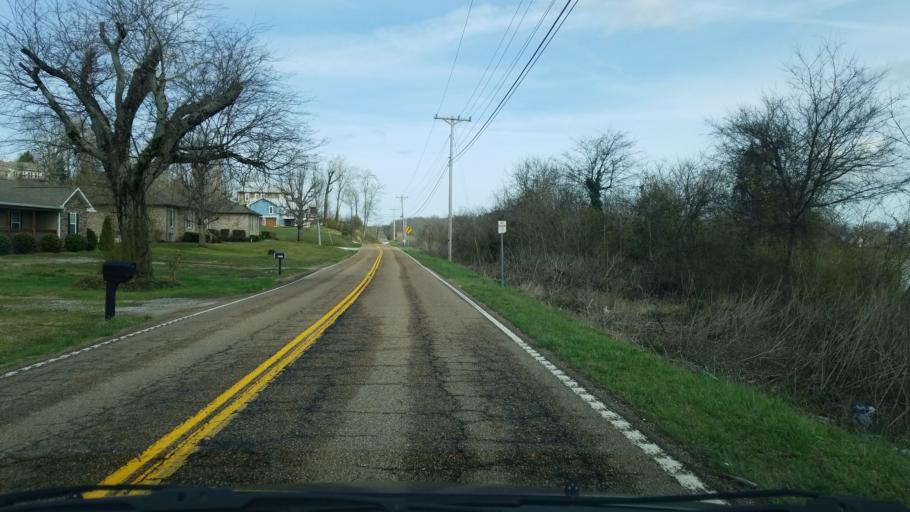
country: US
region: Tennessee
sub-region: Hamilton County
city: Lakesite
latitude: 35.1537
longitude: -85.0616
